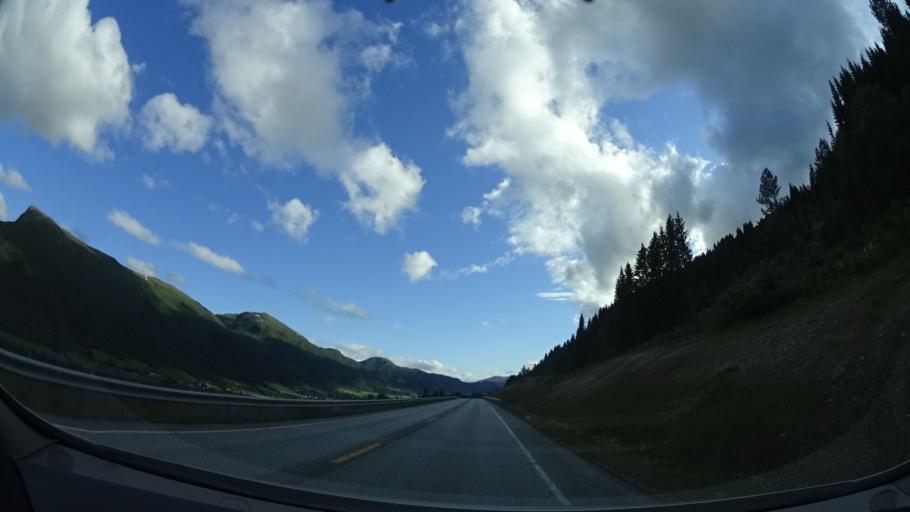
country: NO
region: More og Romsdal
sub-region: Gjemnes
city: Batnfjordsora
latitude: 62.9147
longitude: 7.6908
